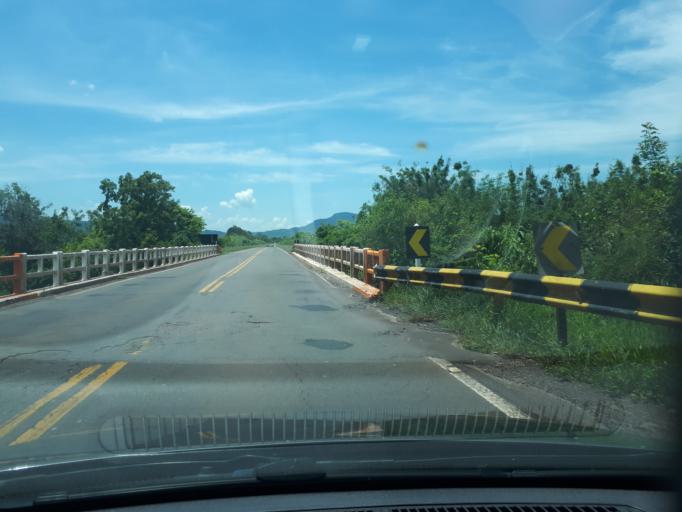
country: BR
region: Rio Grande do Sul
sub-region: Candelaria
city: Candelaria
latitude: -29.7273
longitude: -52.9351
